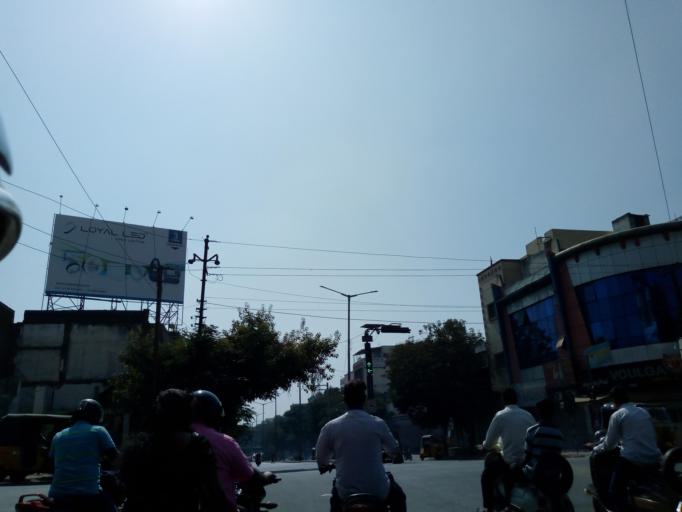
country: IN
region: Telangana
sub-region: Hyderabad
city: Malkajgiri
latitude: 17.4334
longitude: 78.4931
